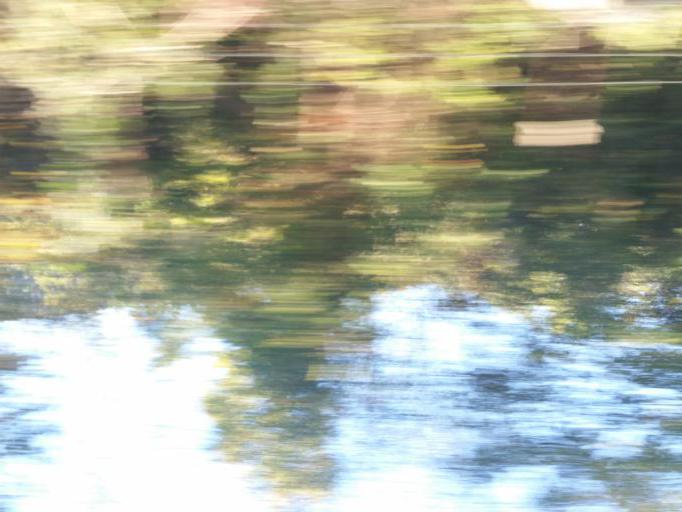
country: US
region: Tennessee
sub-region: Grainger County
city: Rutledge
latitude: 36.3420
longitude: -83.4753
